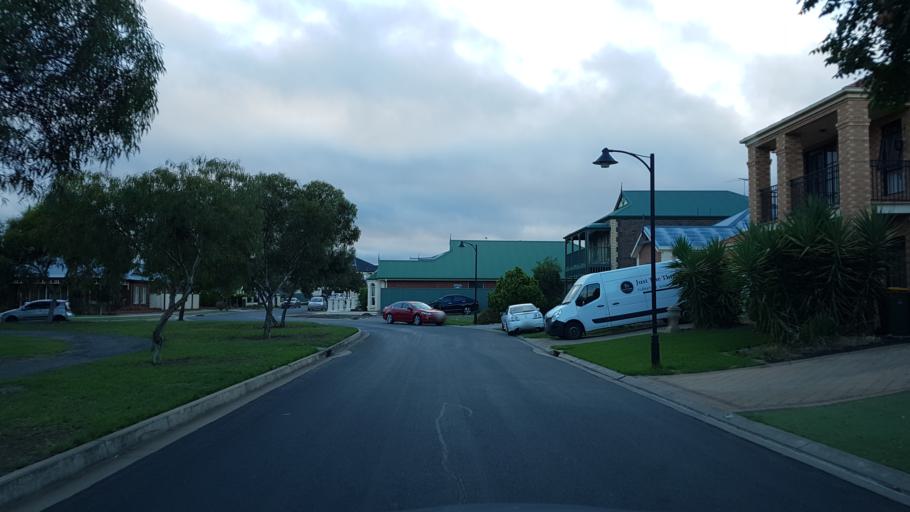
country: AU
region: South Australia
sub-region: Salisbury
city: Ingle Farm
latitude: -34.8118
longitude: 138.6062
